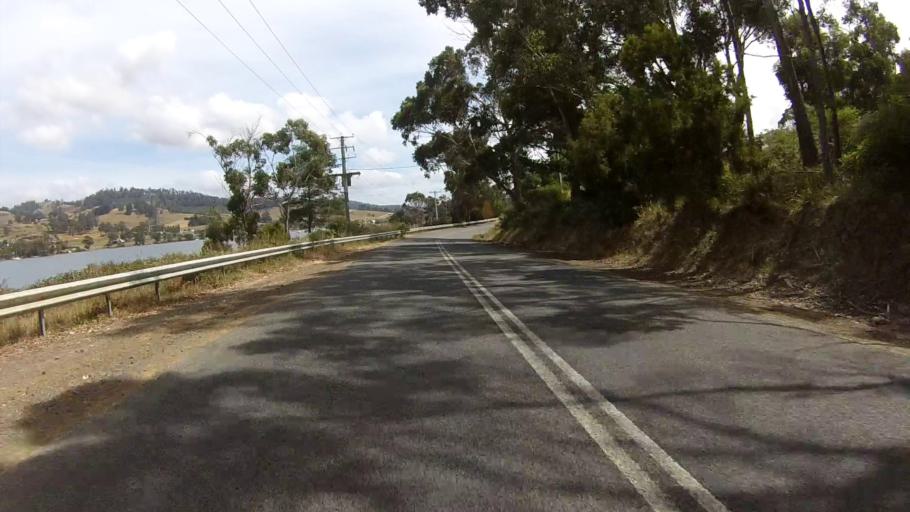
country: AU
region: Tasmania
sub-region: Huon Valley
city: Cygnet
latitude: -43.1813
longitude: 147.0935
